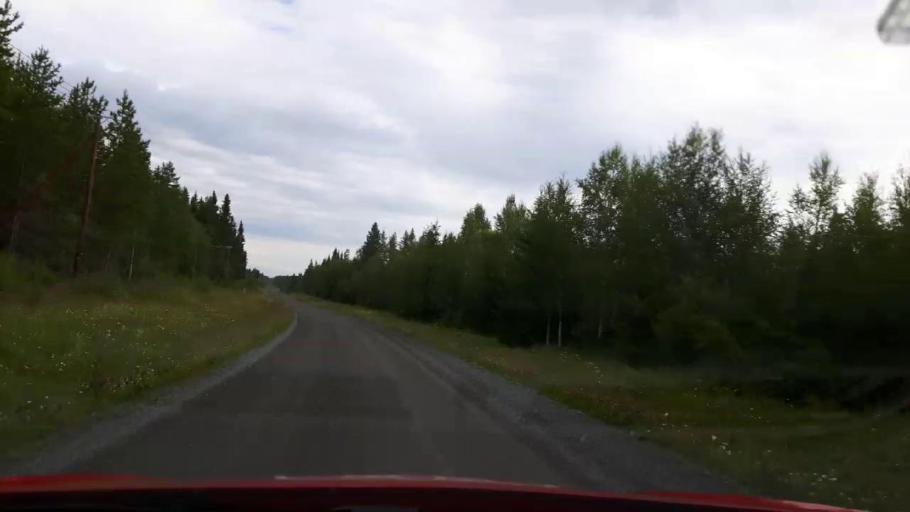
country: SE
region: Jaemtland
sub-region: Stroemsunds Kommun
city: Stroemsund
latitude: 63.5002
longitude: 15.3295
